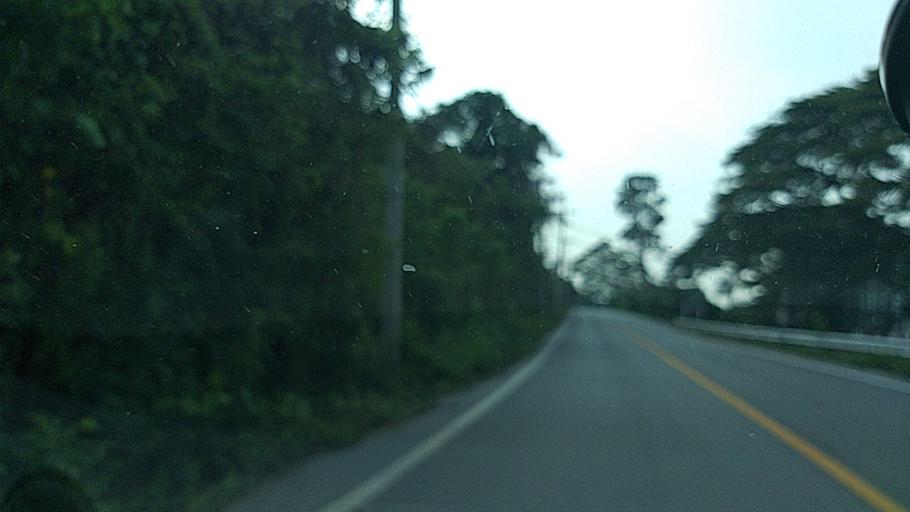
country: TH
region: Sara Buri
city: Saraburi
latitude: 14.4548
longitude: 100.9517
